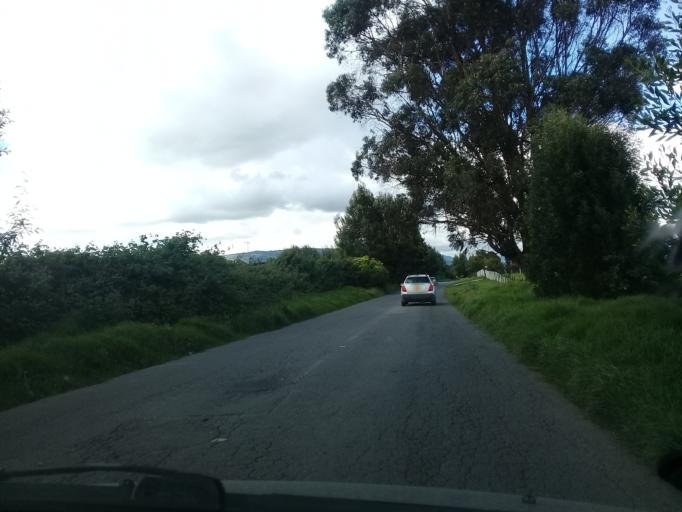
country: CO
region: Cundinamarca
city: Subachoque
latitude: 4.8999
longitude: -74.1933
